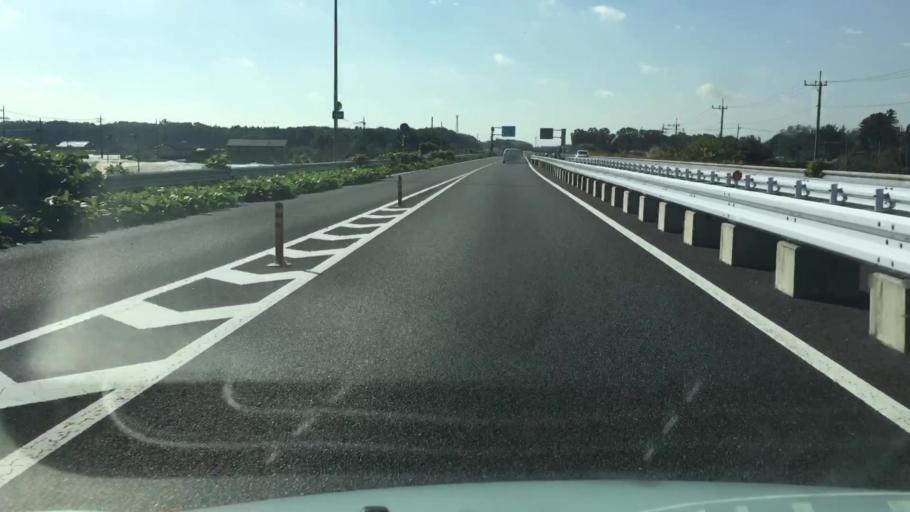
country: JP
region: Tochigi
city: Mooka
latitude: 36.5069
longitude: 139.9877
